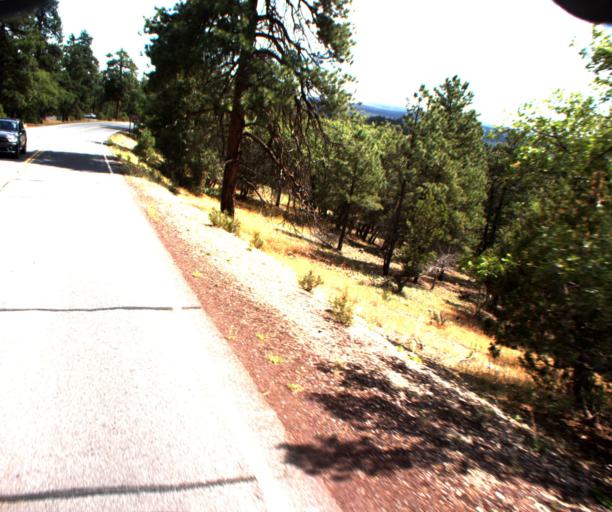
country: US
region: Arizona
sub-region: Coconino County
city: Grand Canyon
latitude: 35.9776
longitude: -111.9567
